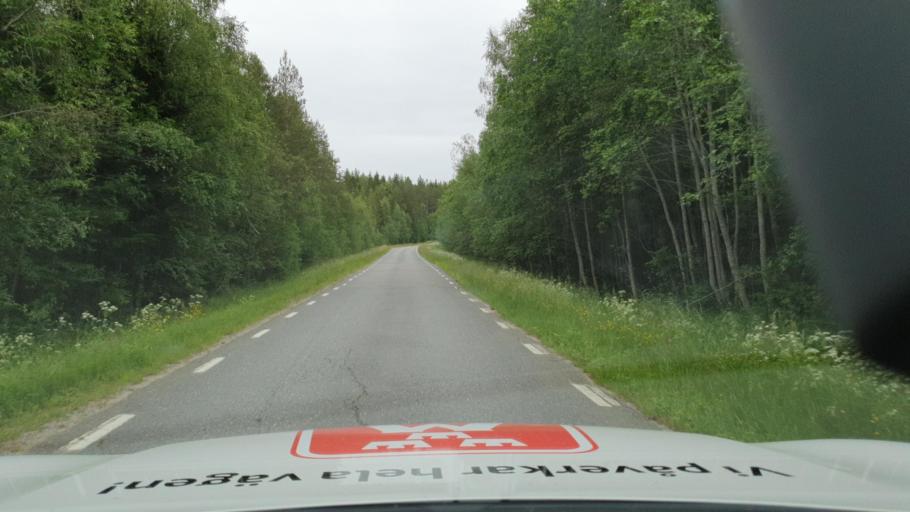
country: SE
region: Vaesterbotten
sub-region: Nordmalings Kommun
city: Nordmaling
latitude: 63.4814
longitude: 19.4534
